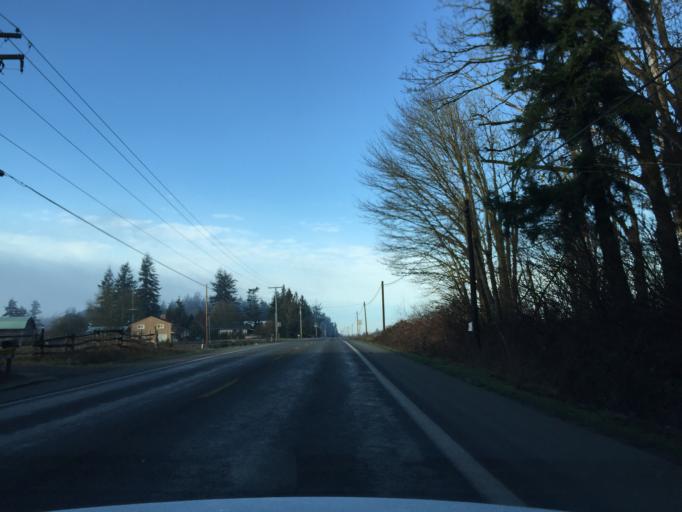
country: US
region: Washington
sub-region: Whatcom County
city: Lynden
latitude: 48.9356
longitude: -122.4977
